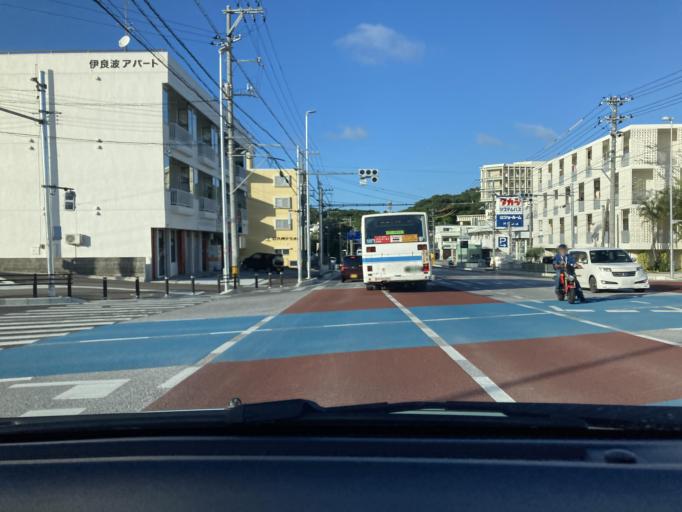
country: JP
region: Okinawa
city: Naha-shi
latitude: 26.2043
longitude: 127.7216
